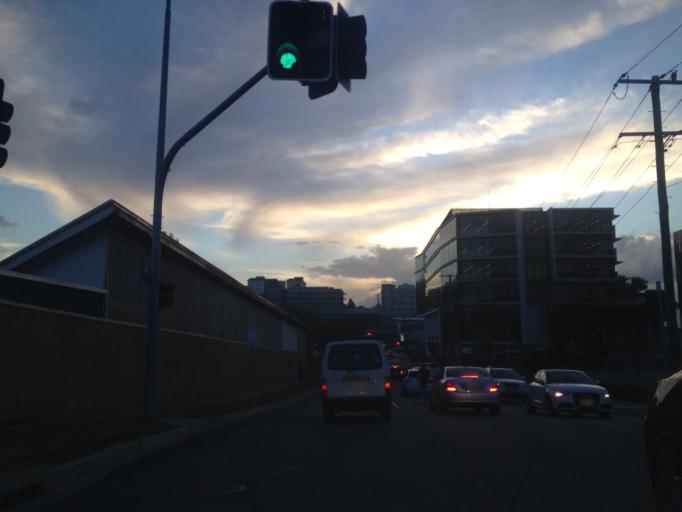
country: AU
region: Queensland
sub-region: Brisbane
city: Fortitude Valley
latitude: -27.4484
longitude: 153.0330
